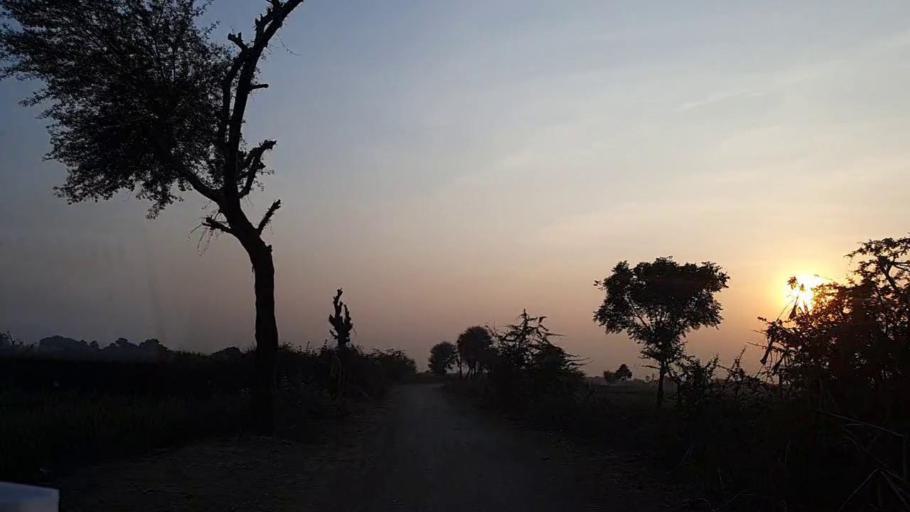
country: PK
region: Sindh
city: Tando Ghulam Ali
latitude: 25.1718
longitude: 68.9268
